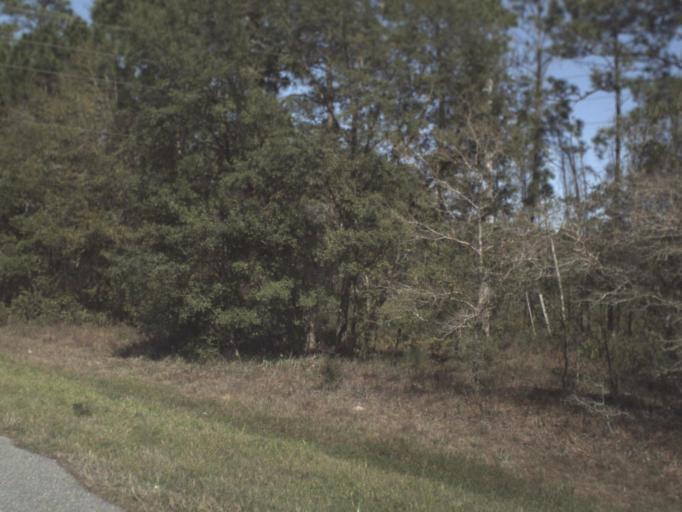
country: US
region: Florida
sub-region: Wakulla County
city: Crawfordville
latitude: 29.9437
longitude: -84.3867
